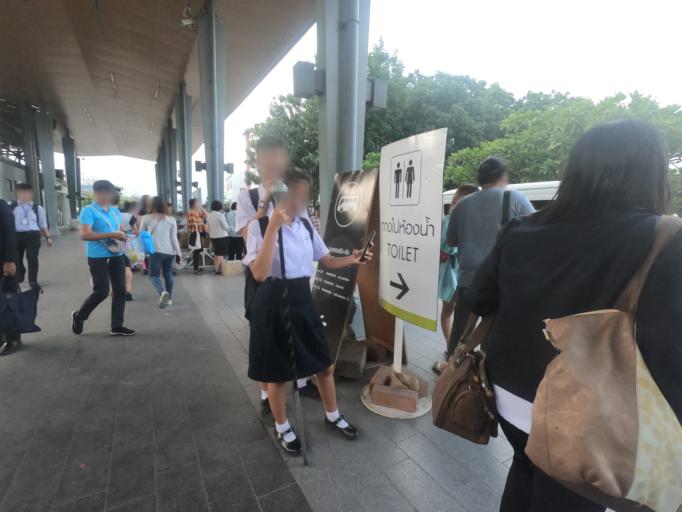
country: TH
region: Bangkok
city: Sai Mai
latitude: 13.9627
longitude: 100.6567
